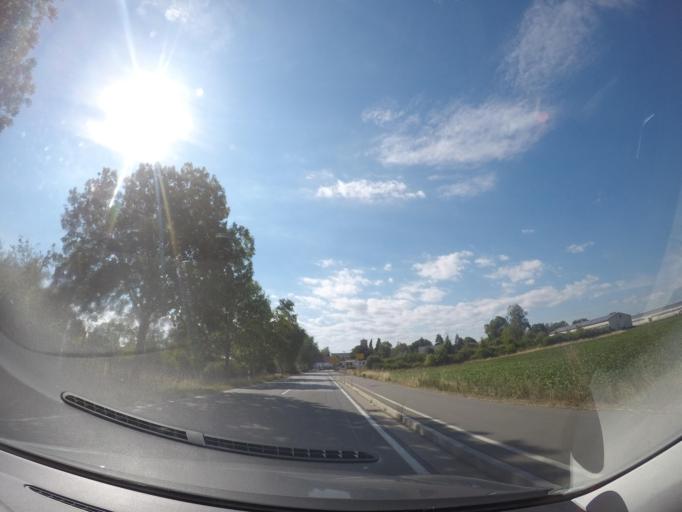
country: DE
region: Saxony-Anhalt
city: Langeln
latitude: 51.9476
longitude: 10.8240
